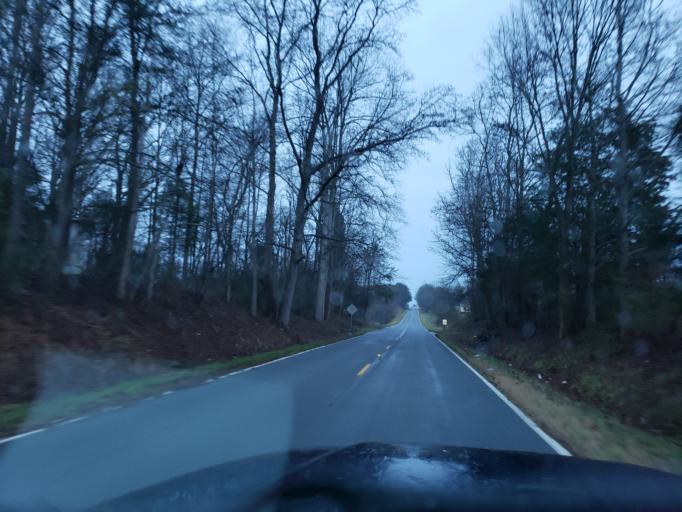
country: US
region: South Carolina
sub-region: Cherokee County
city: Blacksburg
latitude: 35.1408
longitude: -81.4612
